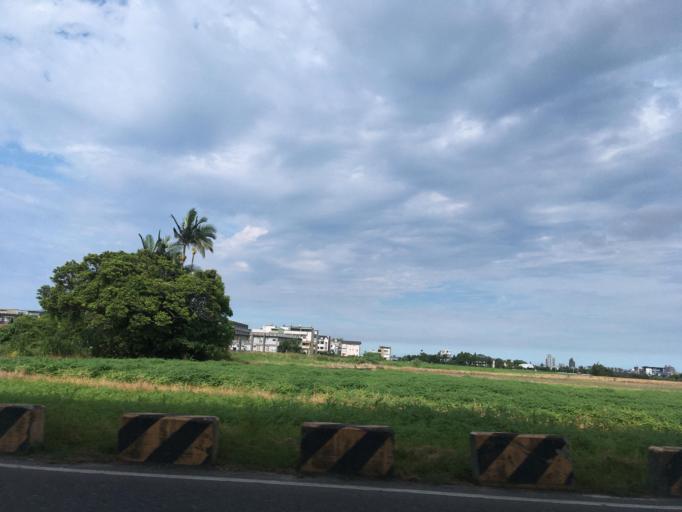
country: TW
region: Taiwan
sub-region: Yilan
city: Yilan
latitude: 24.6821
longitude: 121.7930
